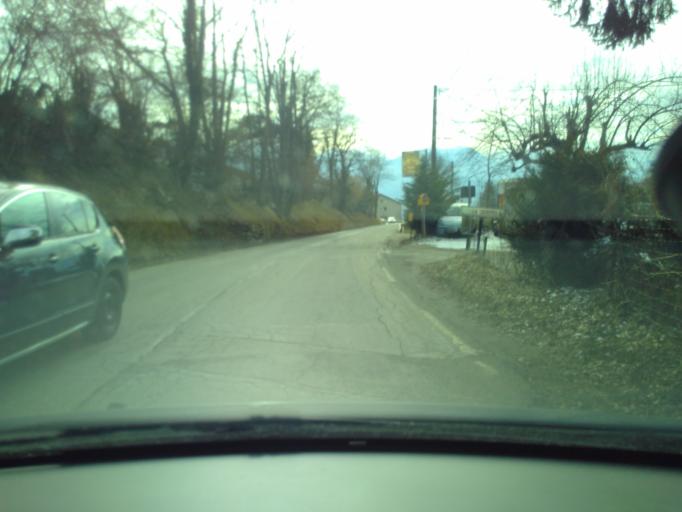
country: FR
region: Rhone-Alpes
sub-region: Departement de l'Isere
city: Corenc
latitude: 45.2331
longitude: 5.7512
